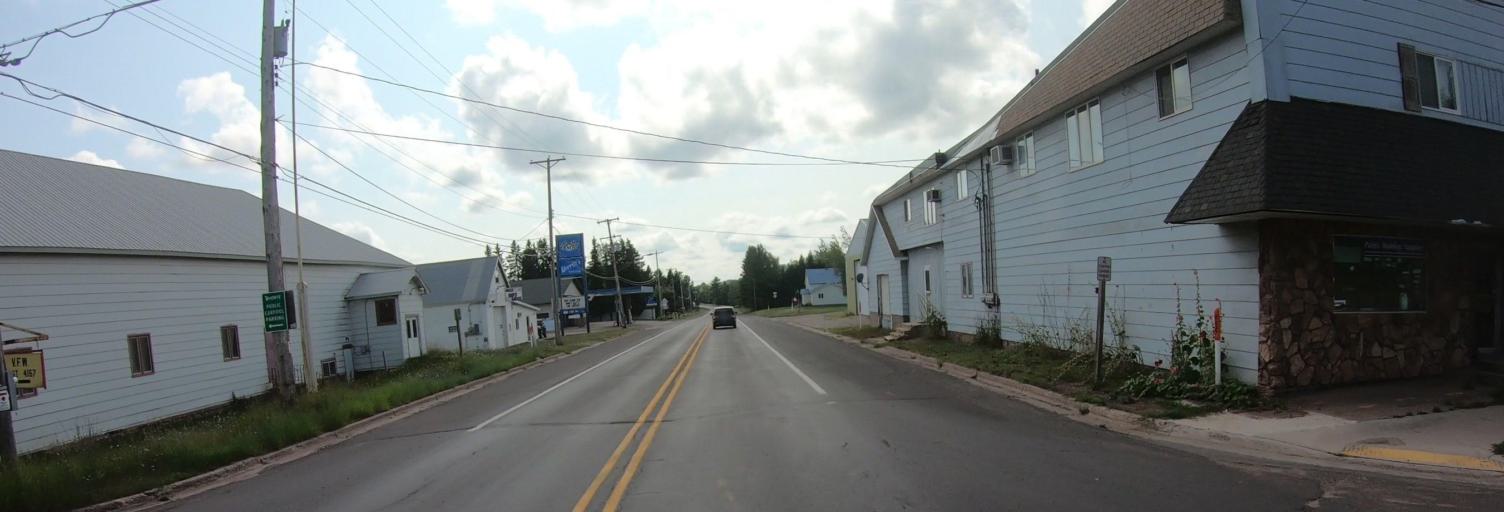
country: US
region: Michigan
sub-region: Ontonagon County
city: Ontonagon
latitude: 46.7619
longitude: -89.0788
